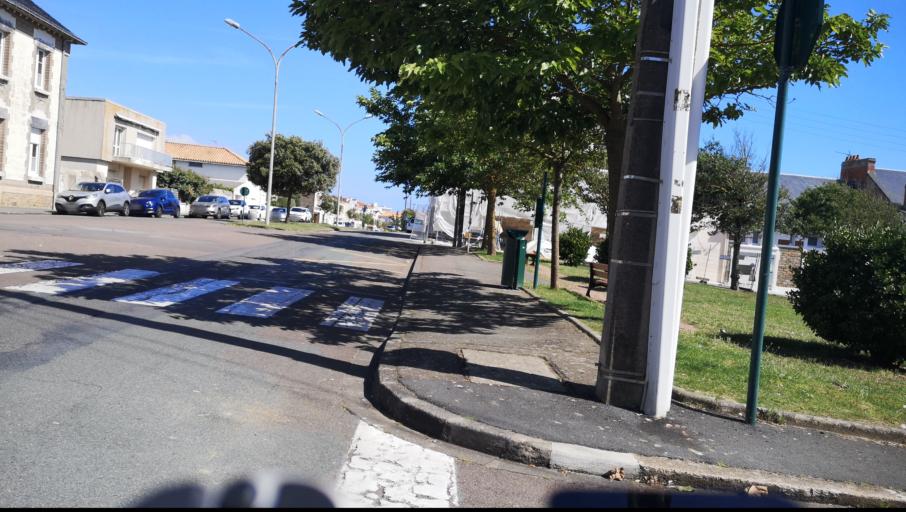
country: FR
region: Pays de la Loire
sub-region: Departement de la Vendee
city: Les Sables-d'Olonne
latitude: 46.4916
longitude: -1.7695
